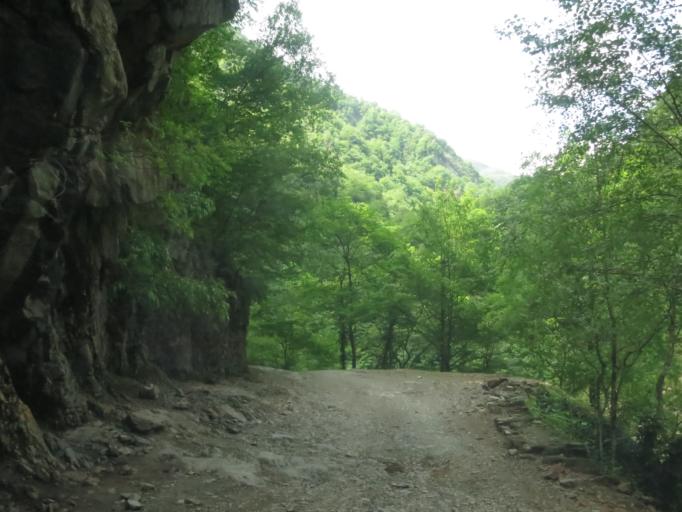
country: GE
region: Kakheti
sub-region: Telavi
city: Telavi
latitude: 42.2133
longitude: 45.4752
